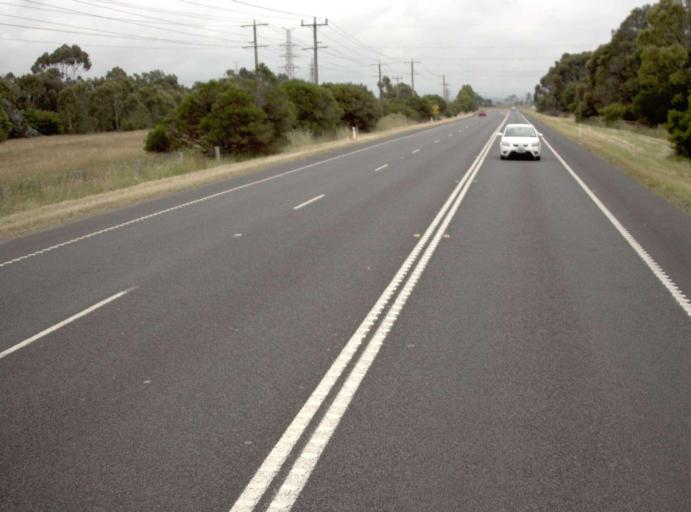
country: AU
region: Victoria
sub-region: Latrobe
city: Morwell
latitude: -38.2736
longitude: 146.4217
